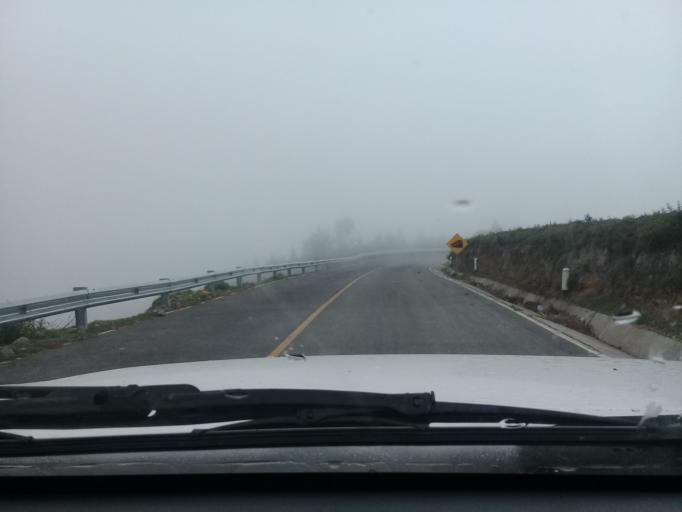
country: MX
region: Veracruz
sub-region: Mariano Escobedo
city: Texmola
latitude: 18.9573
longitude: -97.2211
